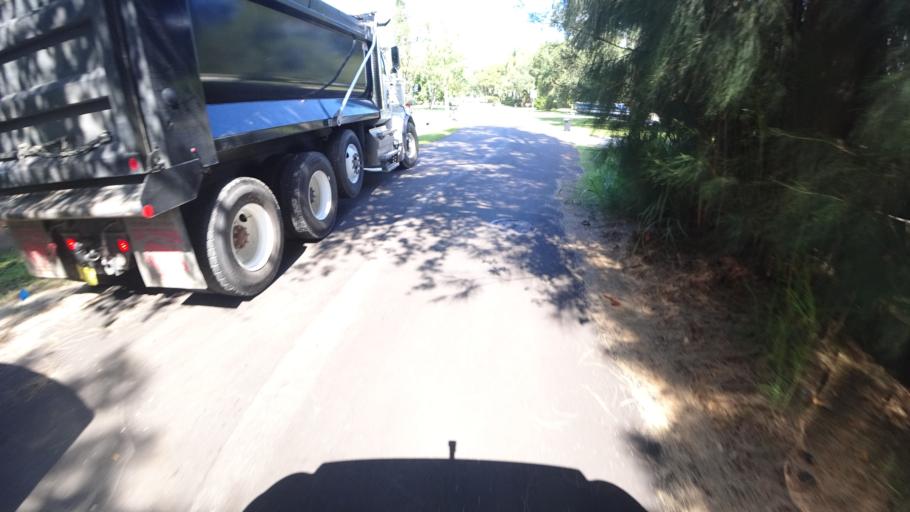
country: US
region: Florida
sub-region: Manatee County
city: Whitfield
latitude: 27.4238
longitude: -82.5529
